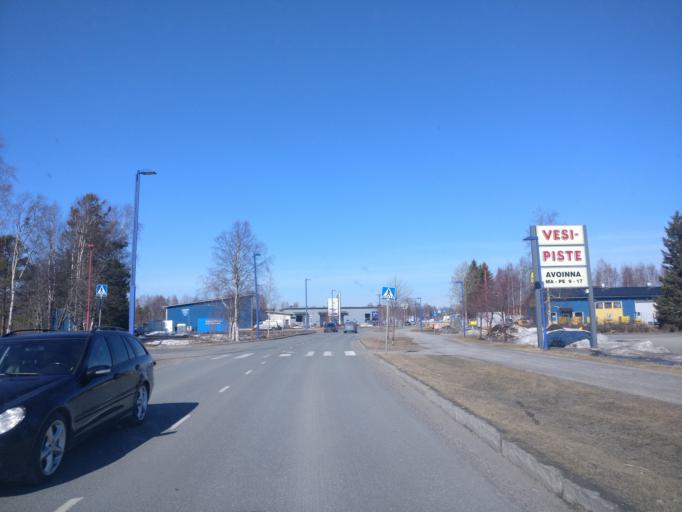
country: FI
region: Lapland
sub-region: Kemi-Tornio
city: Kemi
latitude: 65.7395
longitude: 24.5778
